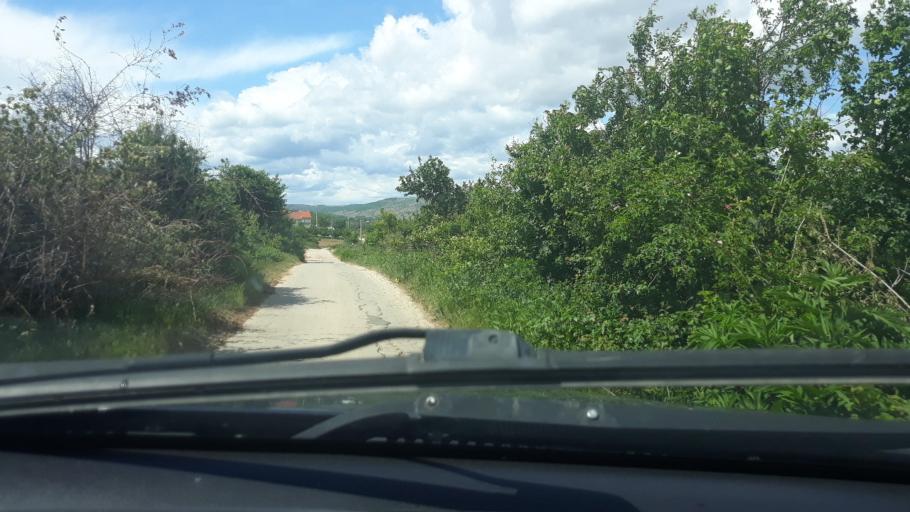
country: MK
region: Krivogastani
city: Krivogashtani
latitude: 41.3343
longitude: 21.3016
